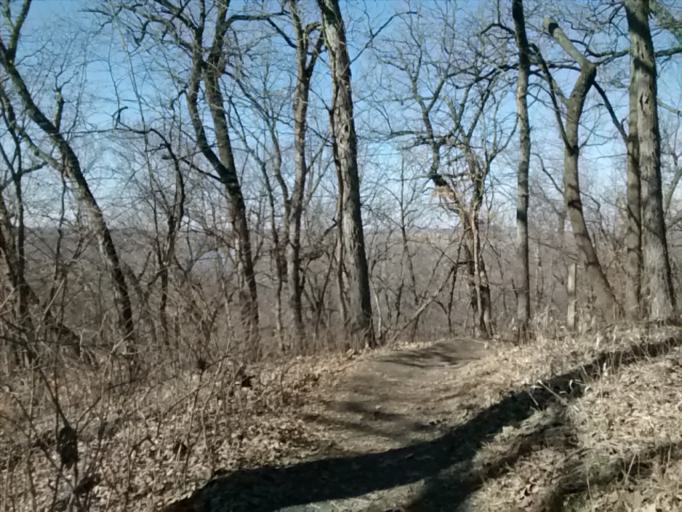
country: US
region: Nebraska
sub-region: Sarpy County
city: Bellevue
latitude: 41.1827
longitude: -95.9173
